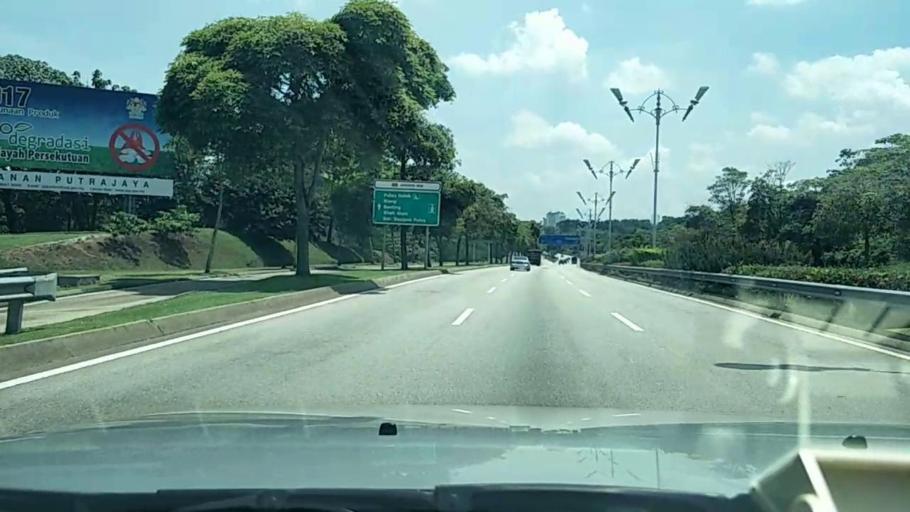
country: MY
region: Putrajaya
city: Putrajaya
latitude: 2.9548
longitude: 101.6957
